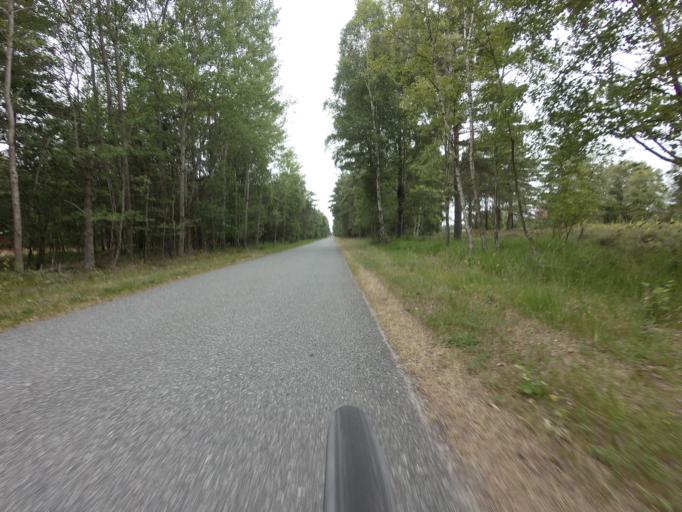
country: DK
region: North Denmark
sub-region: Laeso Kommune
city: Byrum
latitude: 57.2751
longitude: 10.9661
